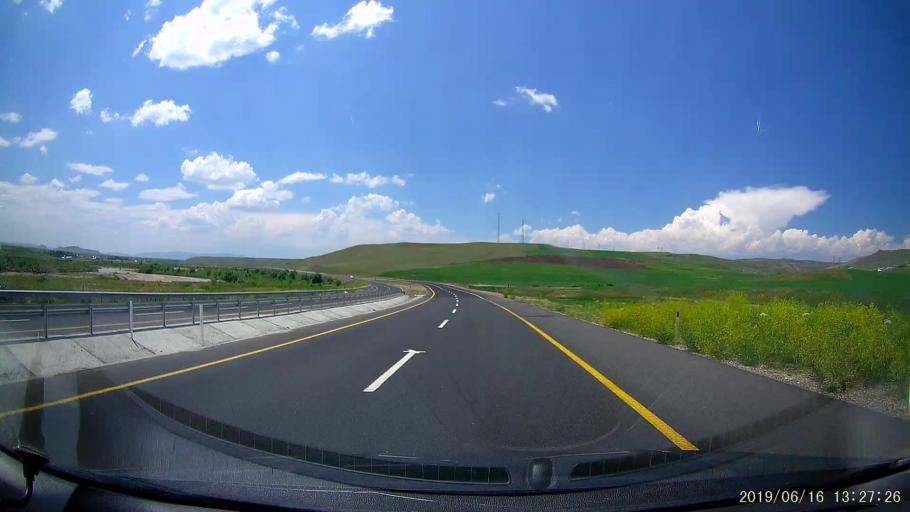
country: TR
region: Agri
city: Taslicay
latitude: 39.6709
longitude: 43.3108
